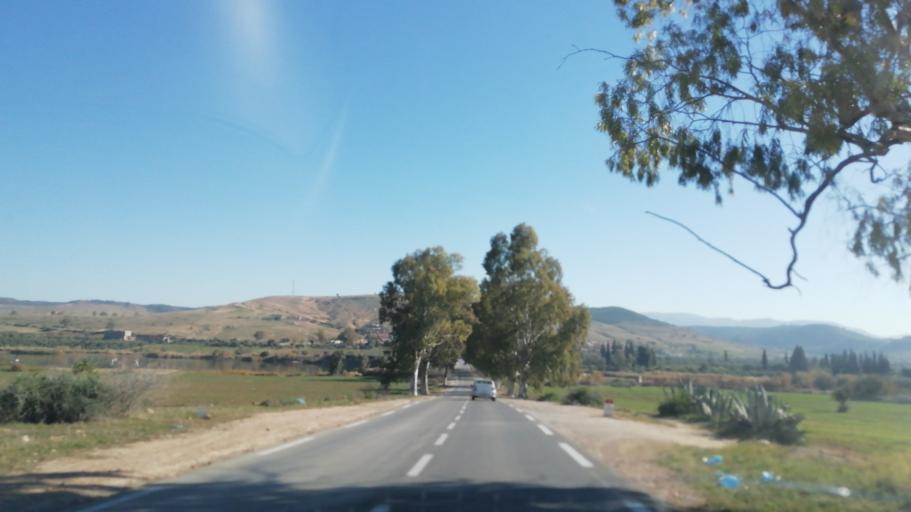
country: DZ
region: Tlemcen
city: Nedroma
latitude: 34.8273
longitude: -1.6584
